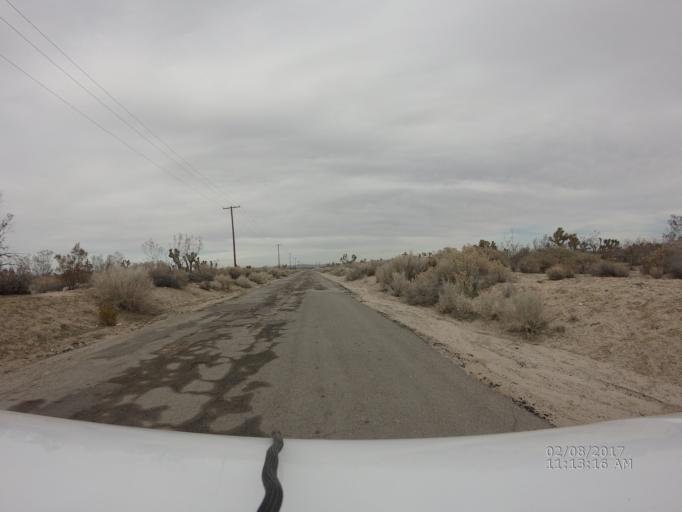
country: US
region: California
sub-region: San Bernardino County
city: Pinon Hills
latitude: 34.4927
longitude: -117.6600
